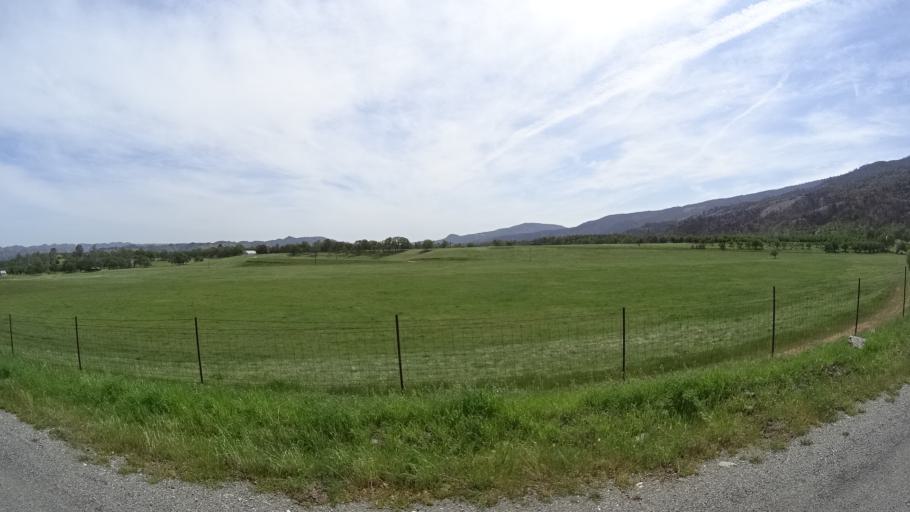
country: US
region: California
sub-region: Glenn County
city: Willows
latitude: 39.5760
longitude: -122.6113
